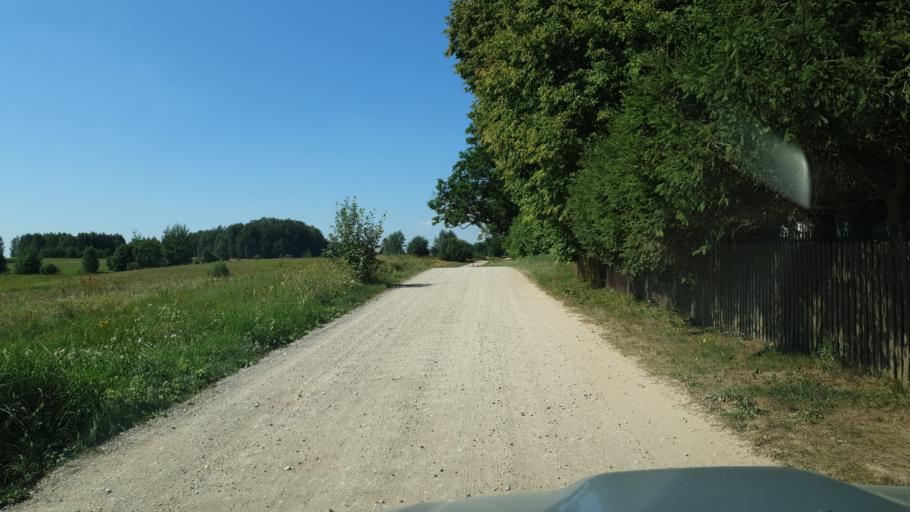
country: LT
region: Vilnius County
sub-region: Vilniaus Rajonas
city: Vievis
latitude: 54.8988
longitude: 24.8702
